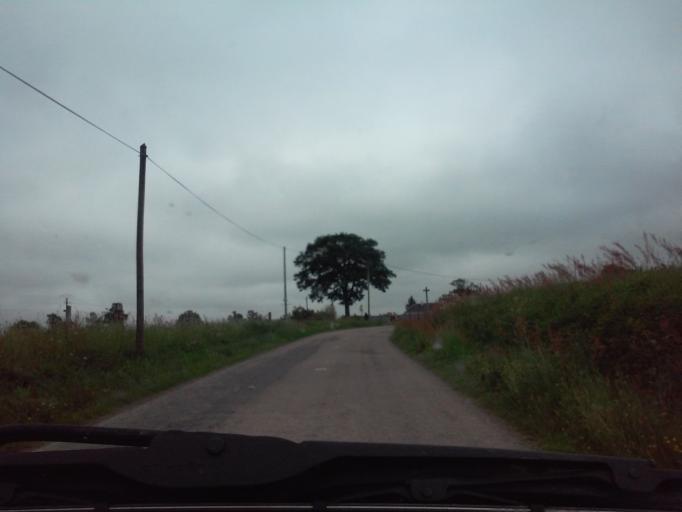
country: FR
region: Pays de la Loire
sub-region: Departement de la Mayenne
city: Ballots
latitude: 47.9614
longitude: -1.0412
